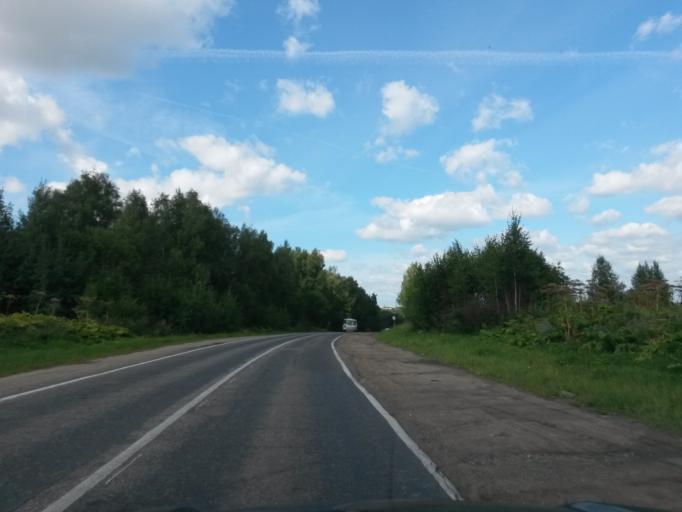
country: RU
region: Jaroslavl
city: Yaroslavl
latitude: 57.5441
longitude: 39.8619
